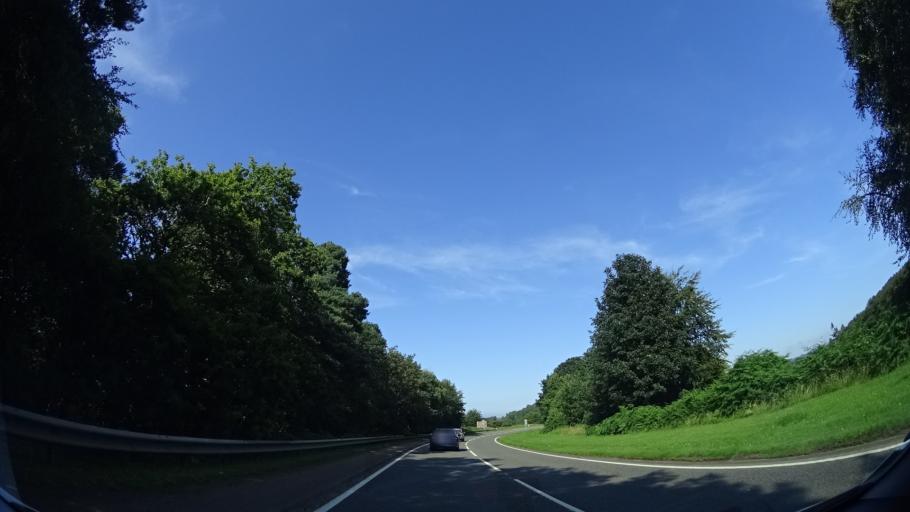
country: GB
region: Scotland
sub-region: Highland
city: Inverness
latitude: 57.4615
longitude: -4.2568
